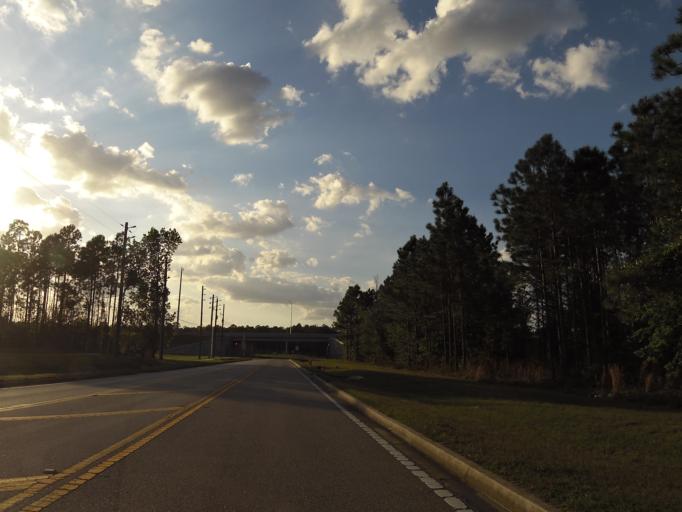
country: US
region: Florida
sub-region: Saint Johns County
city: Fruit Cove
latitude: 30.0806
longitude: -81.5267
